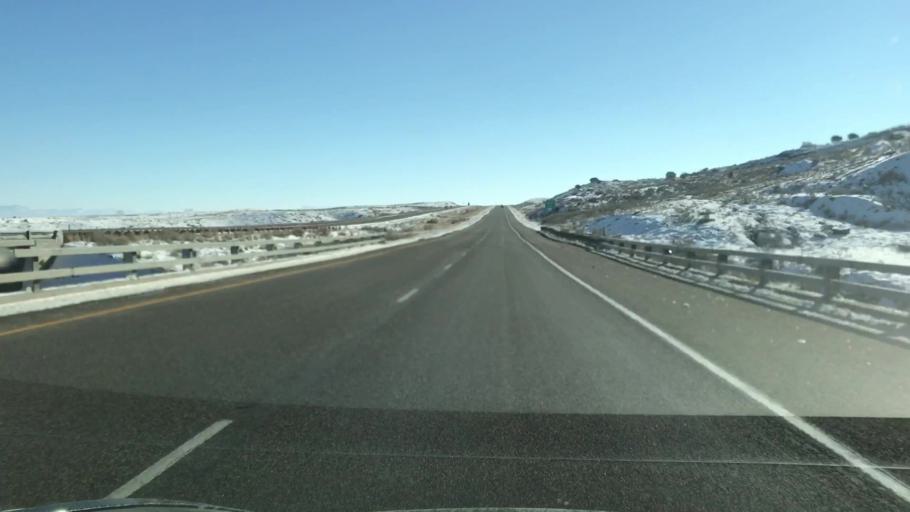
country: US
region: Colorado
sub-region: Mesa County
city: Loma
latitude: 39.2228
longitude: -108.8905
